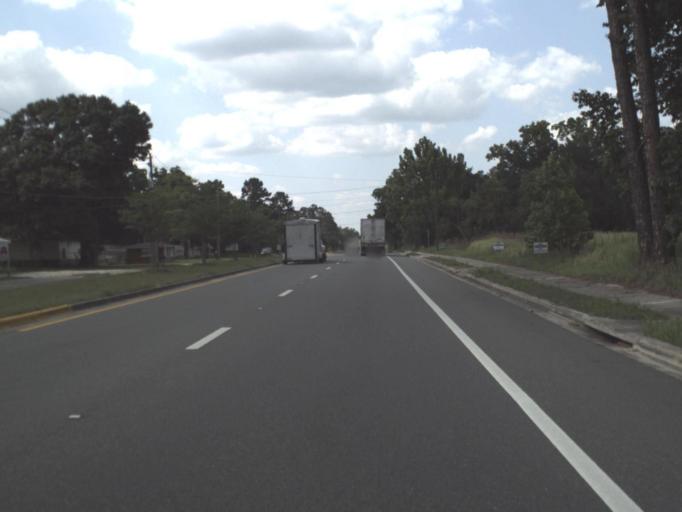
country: US
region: Florida
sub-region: Alachua County
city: Waldo
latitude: 29.7825
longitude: -82.1674
